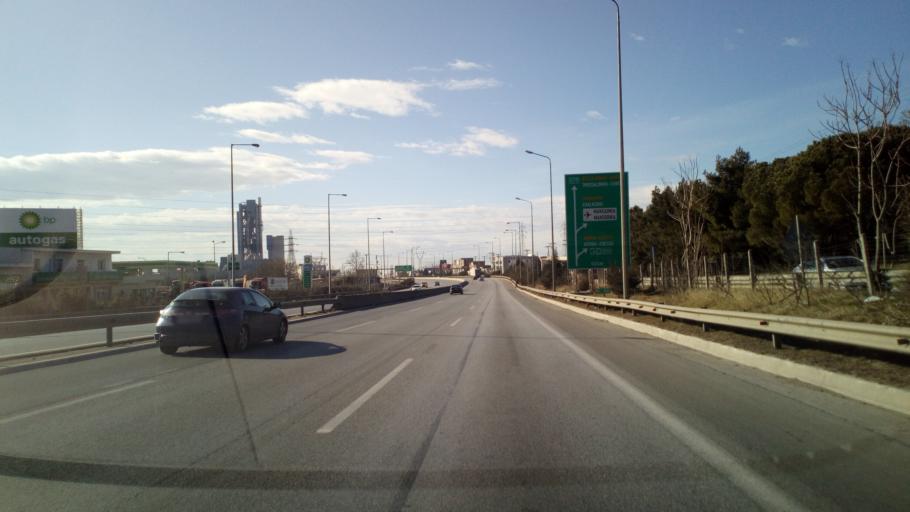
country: GR
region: Central Macedonia
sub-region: Nomos Thessalonikis
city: Efkarpia
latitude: 40.7081
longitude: 22.9546
